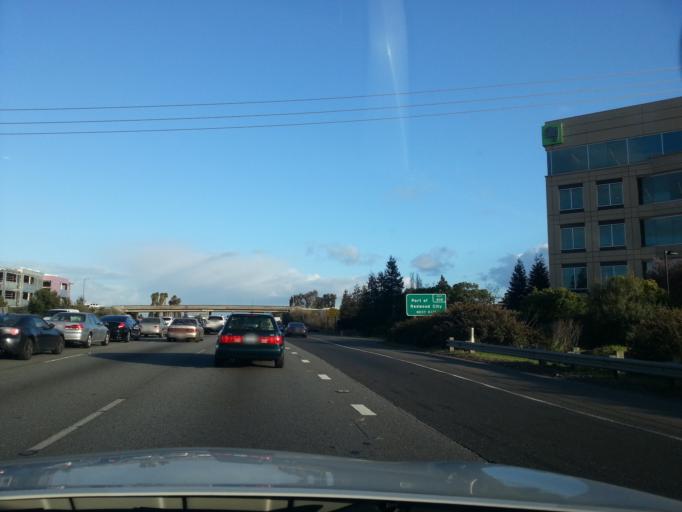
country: US
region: California
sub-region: San Mateo County
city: Redwood City
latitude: 37.4928
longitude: -122.2226
